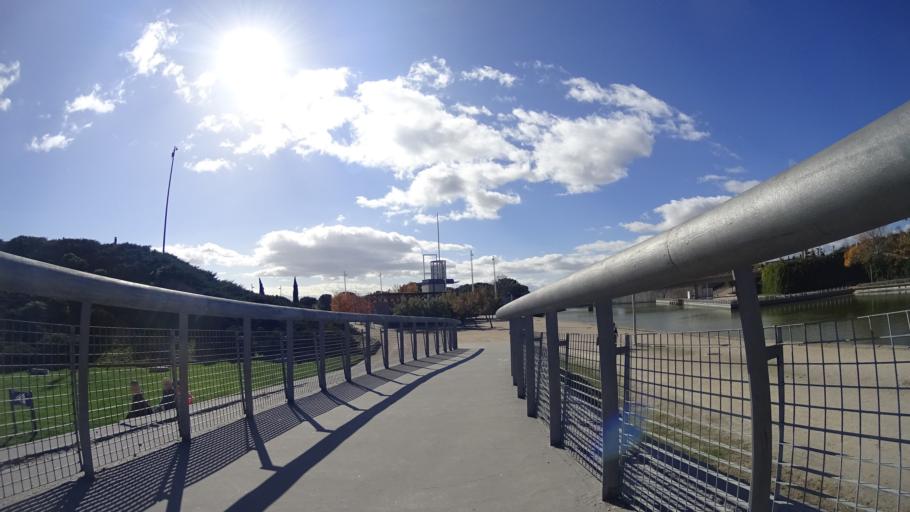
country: ES
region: Madrid
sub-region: Provincia de Madrid
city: San Blas
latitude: 40.4596
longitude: -3.6077
